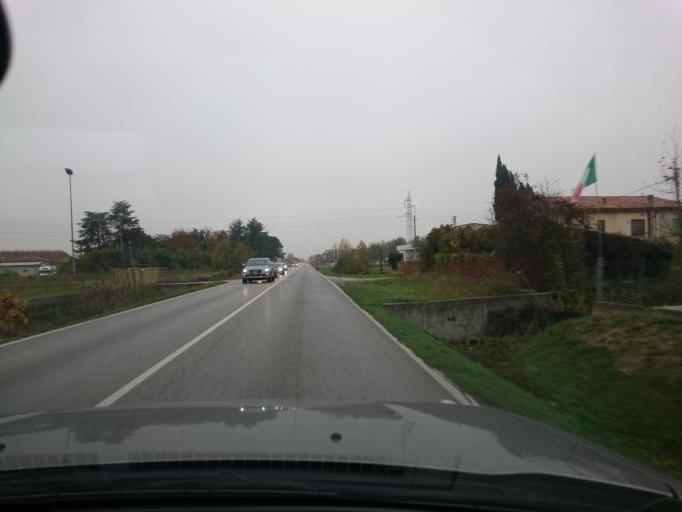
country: IT
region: Veneto
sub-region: Provincia di Padova
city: Legnaro
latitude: 45.3332
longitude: 11.9822
